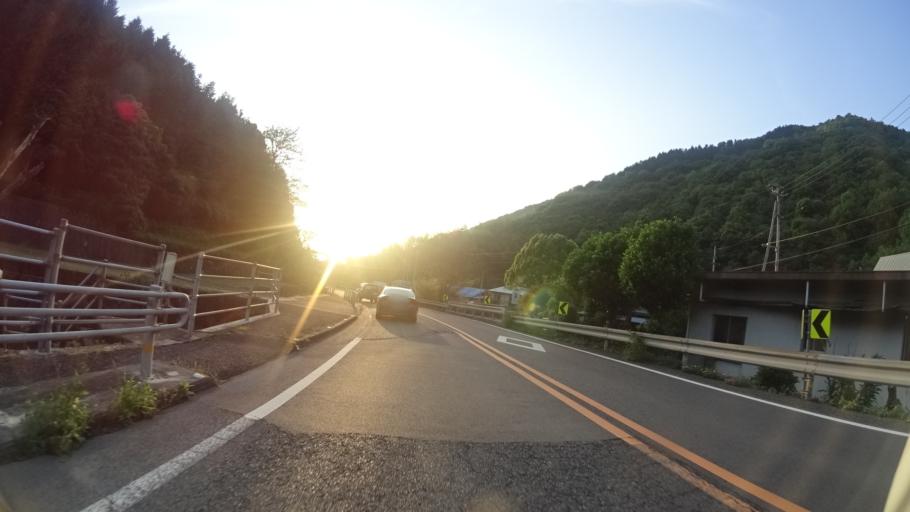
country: JP
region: Ehime
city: Kawanoecho
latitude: 33.9905
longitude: 133.6309
